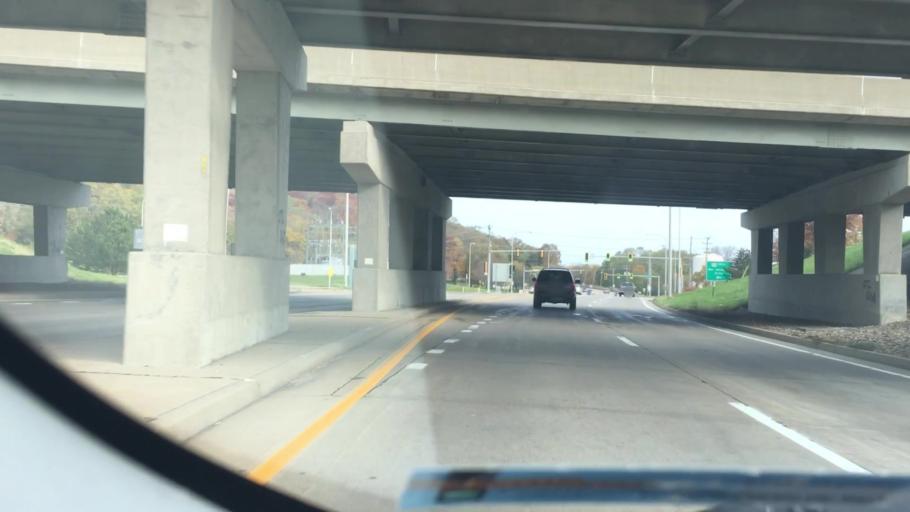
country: US
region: Illinois
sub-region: Peoria County
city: North Peoria
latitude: 40.7230
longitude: -89.5554
